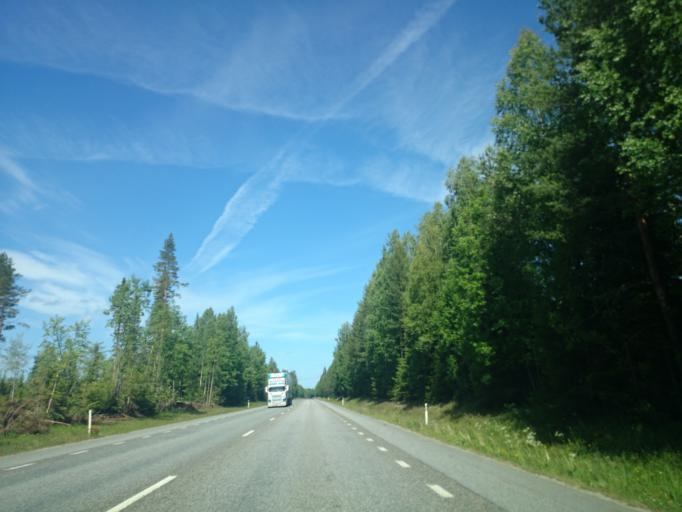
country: SE
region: Jaemtland
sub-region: Braecke Kommun
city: Braecke
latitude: 62.7208
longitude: 15.4507
